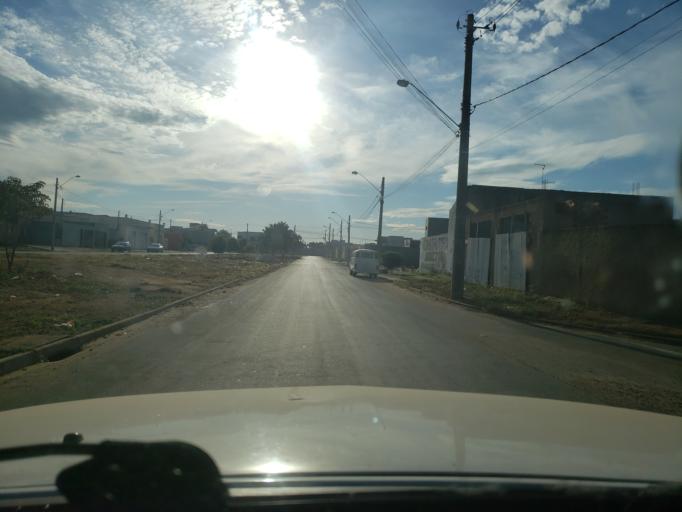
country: BR
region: Sao Paulo
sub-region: Moji-Guacu
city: Mogi-Gaucu
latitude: -22.3243
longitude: -46.9338
